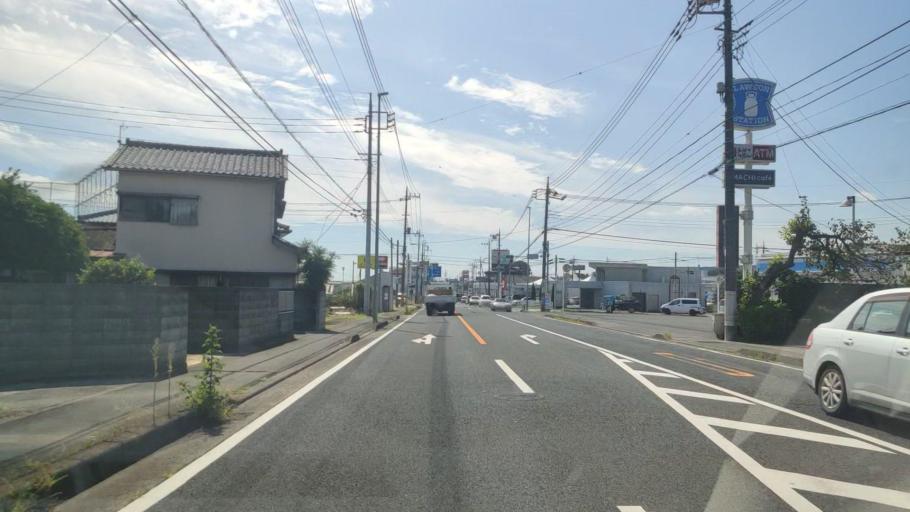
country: JP
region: Gunma
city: Shibukawa
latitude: 36.5123
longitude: 139.0054
